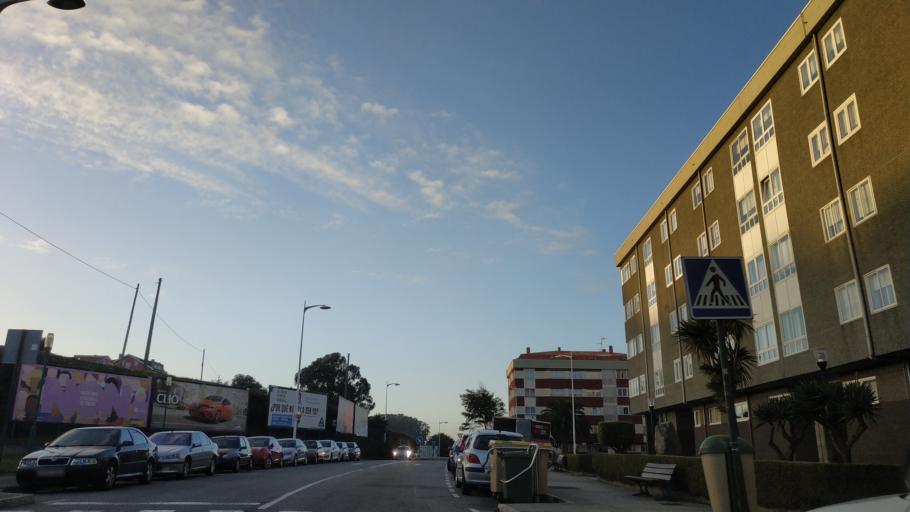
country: ES
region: Galicia
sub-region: Provincia da Coruna
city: A Coruna
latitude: 43.3592
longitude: -8.4264
